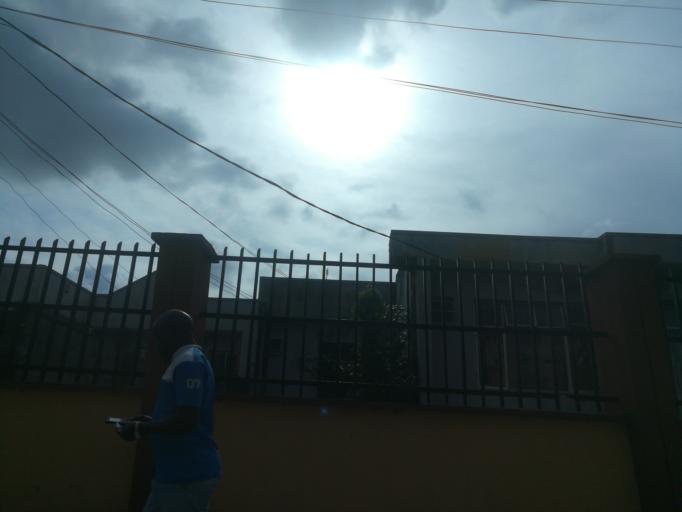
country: NG
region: Lagos
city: Ikeja
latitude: 6.6217
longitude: 3.3608
